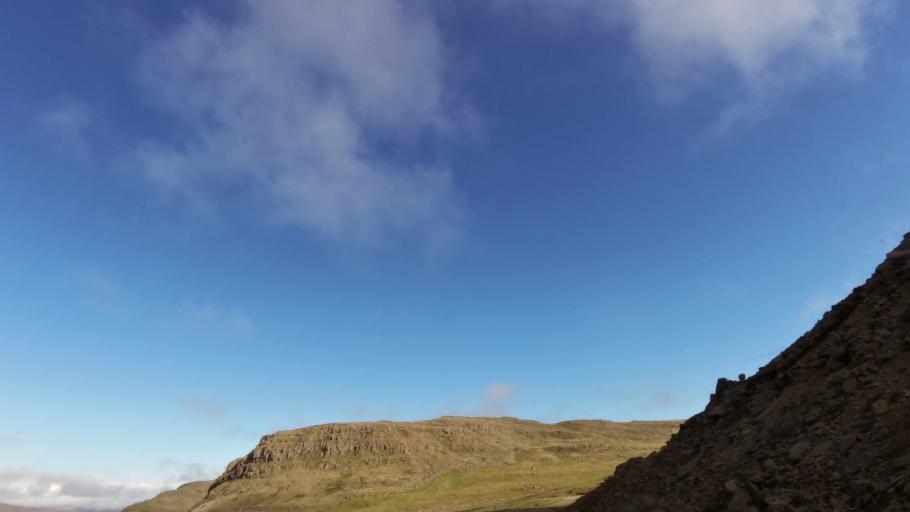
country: IS
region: West
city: Olafsvik
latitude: 65.5635
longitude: -24.0371
